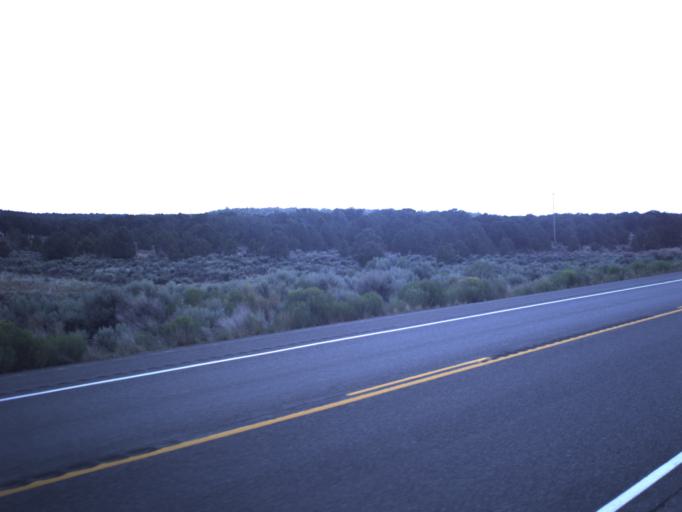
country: US
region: Utah
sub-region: Duchesne County
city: Duchesne
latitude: 40.1814
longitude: -110.6420
